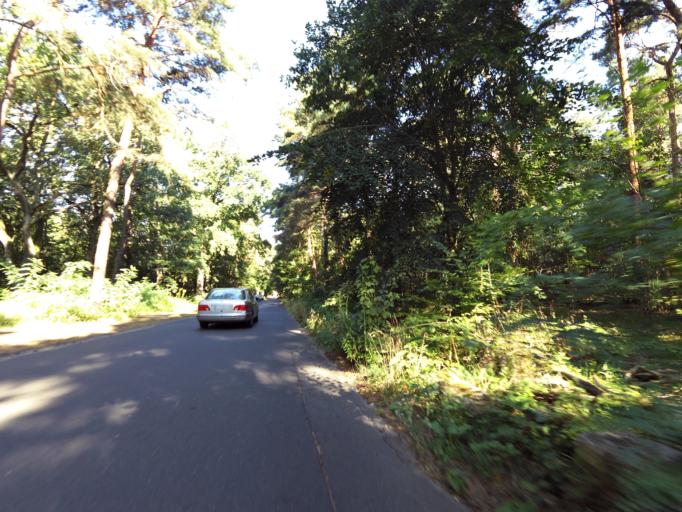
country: DE
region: Berlin
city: Nikolassee
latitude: 52.4364
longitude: 13.1834
